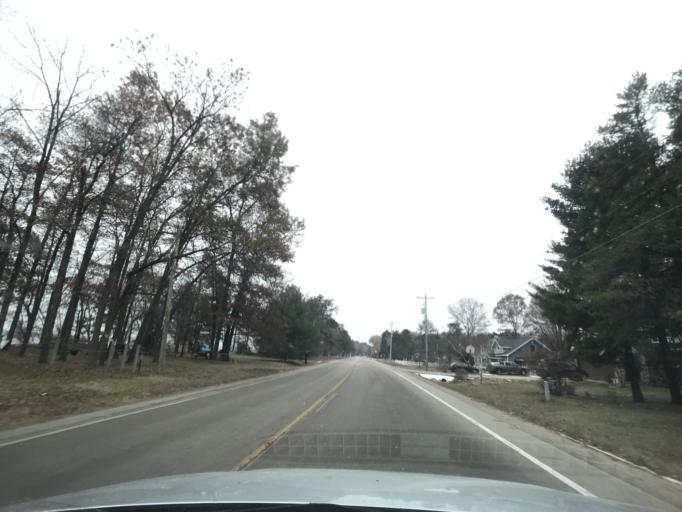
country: US
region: Wisconsin
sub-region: Marinette County
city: Marinette
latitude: 45.0494
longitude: -87.6251
